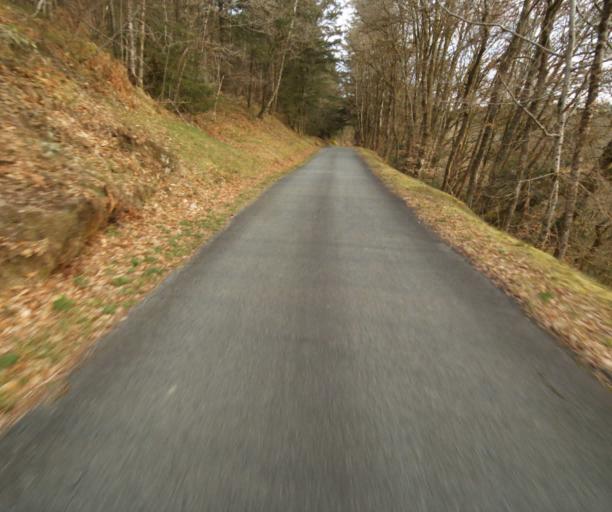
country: FR
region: Limousin
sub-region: Departement de la Correze
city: Correze
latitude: 45.3912
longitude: 1.8881
